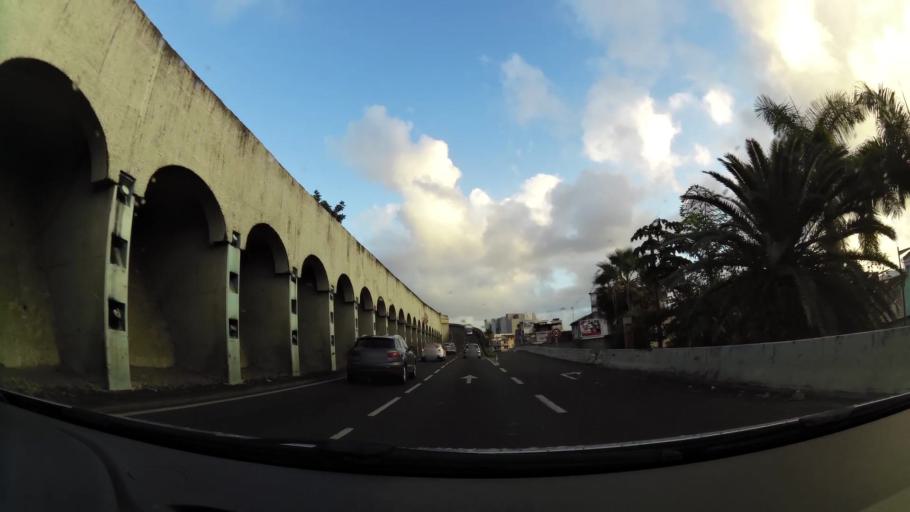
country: MQ
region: Martinique
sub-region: Martinique
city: Fort-de-France
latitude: 14.6104
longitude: -61.0691
